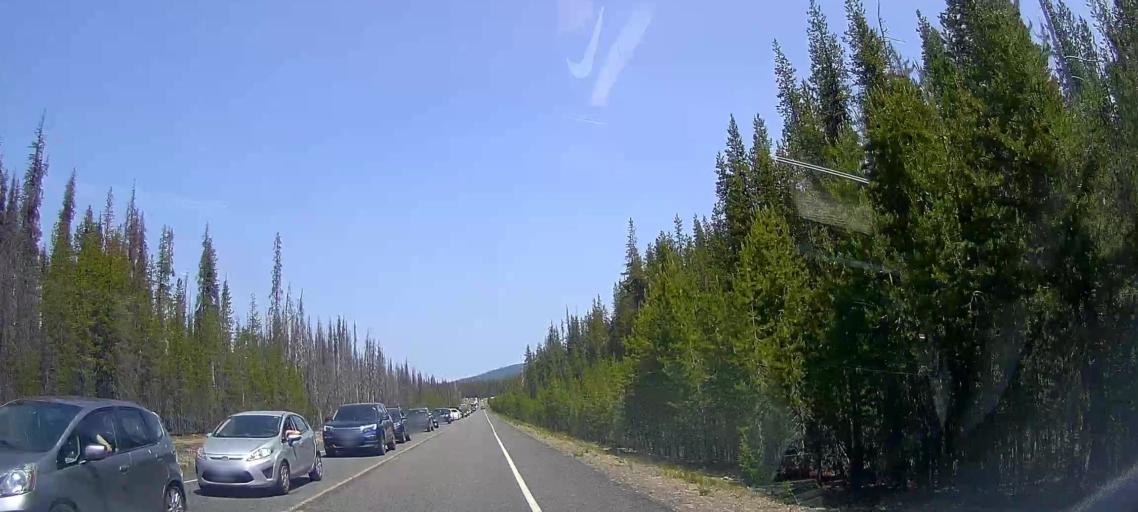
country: US
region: Oregon
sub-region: Lane County
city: Oakridge
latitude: 43.0801
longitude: -122.1178
